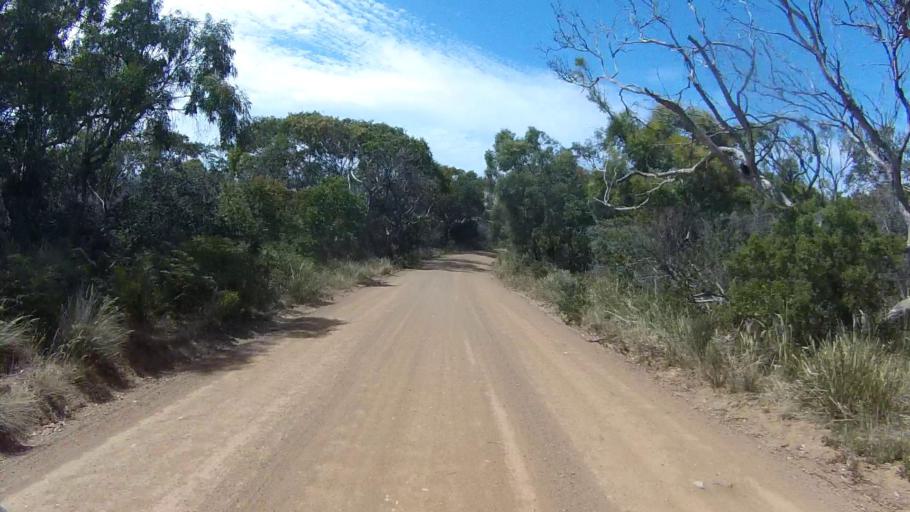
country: AU
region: Tasmania
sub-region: Clarence
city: Sandford
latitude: -43.0213
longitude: 147.4907
